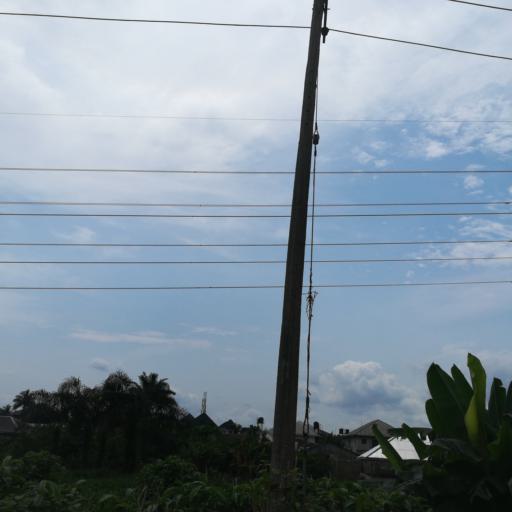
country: NG
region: Rivers
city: Port Harcourt
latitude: 4.8653
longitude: 7.0186
